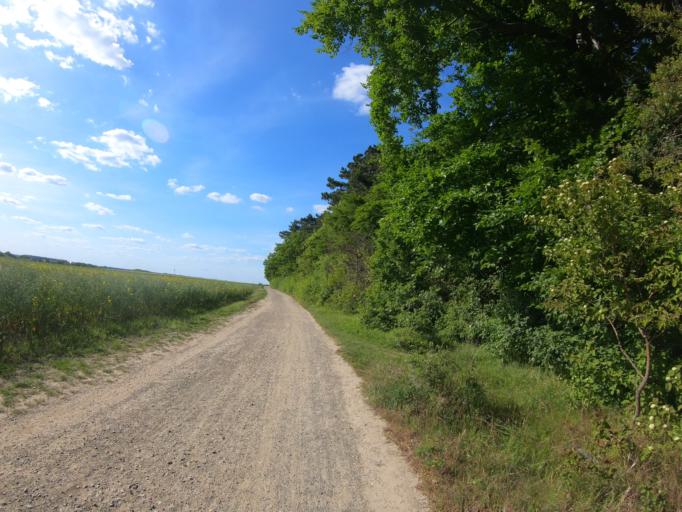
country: DE
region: Lower Saxony
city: Leiferde
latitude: 52.1891
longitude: 10.5281
